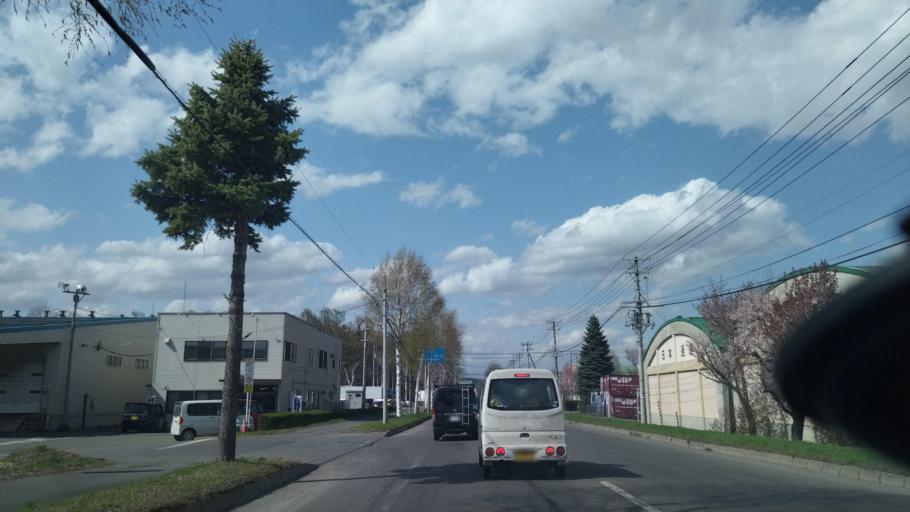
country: JP
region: Hokkaido
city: Obihiro
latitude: 42.9262
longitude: 143.1433
